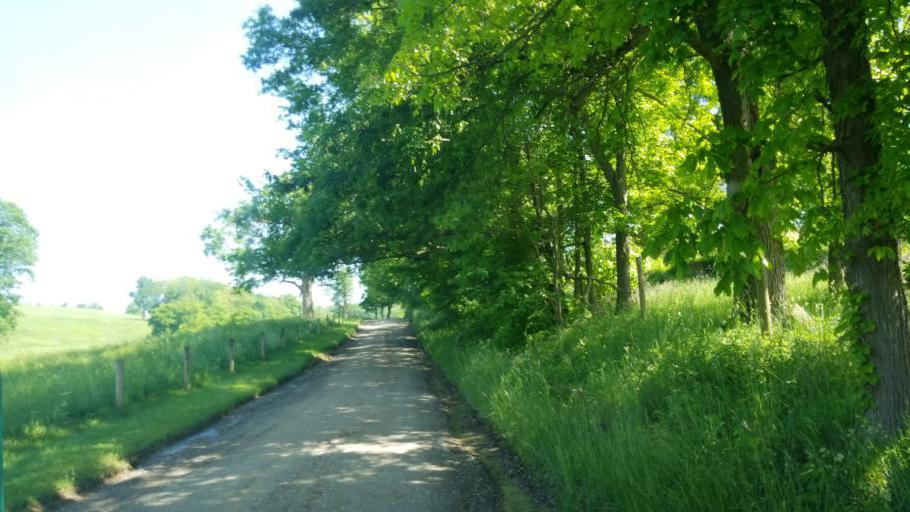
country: US
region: Ohio
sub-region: Holmes County
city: Millersburg
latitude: 40.4404
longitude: -81.8102
